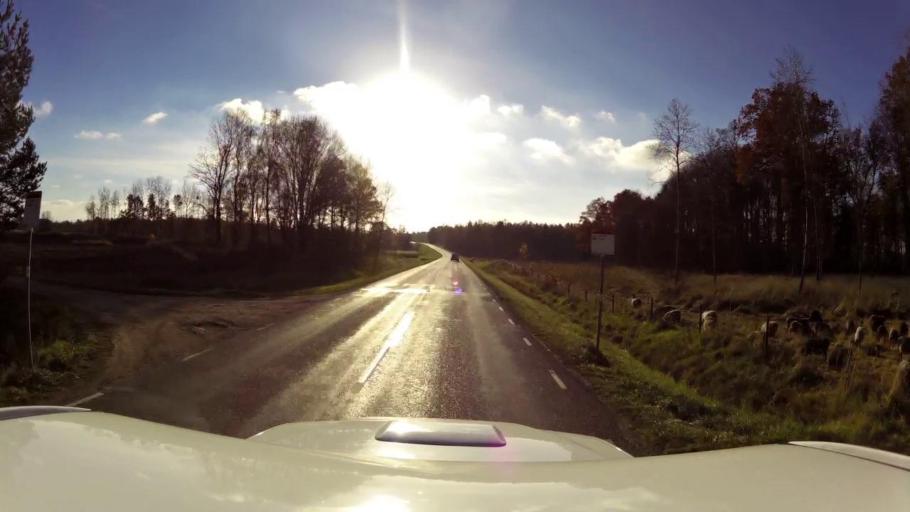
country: SE
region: OEstergoetland
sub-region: Linkopings Kommun
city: Malmslatt
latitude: 58.3428
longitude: 15.5186
